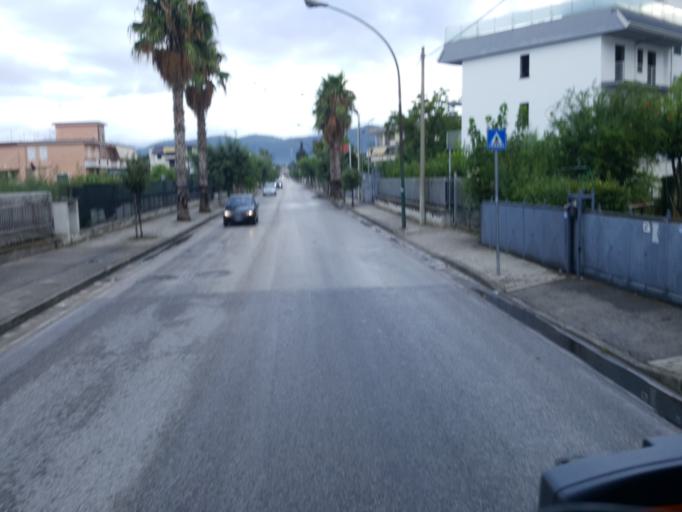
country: IT
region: Campania
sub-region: Provincia di Napoli
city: Palma Campania
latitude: 40.8720
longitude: 14.5479
